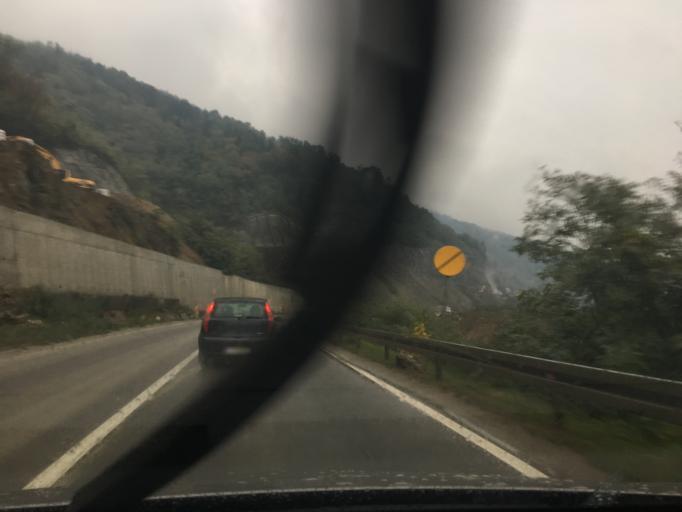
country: RS
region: Central Serbia
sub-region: Pcinjski Okrug
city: Vladicin Han
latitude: 42.7669
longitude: 22.0850
